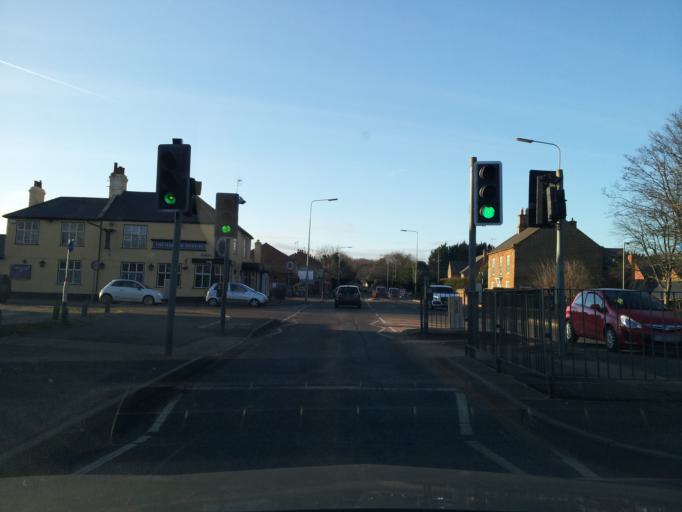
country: GB
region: England
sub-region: Northamptonshire
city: Northampton
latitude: 52.2598
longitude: -0.9519
